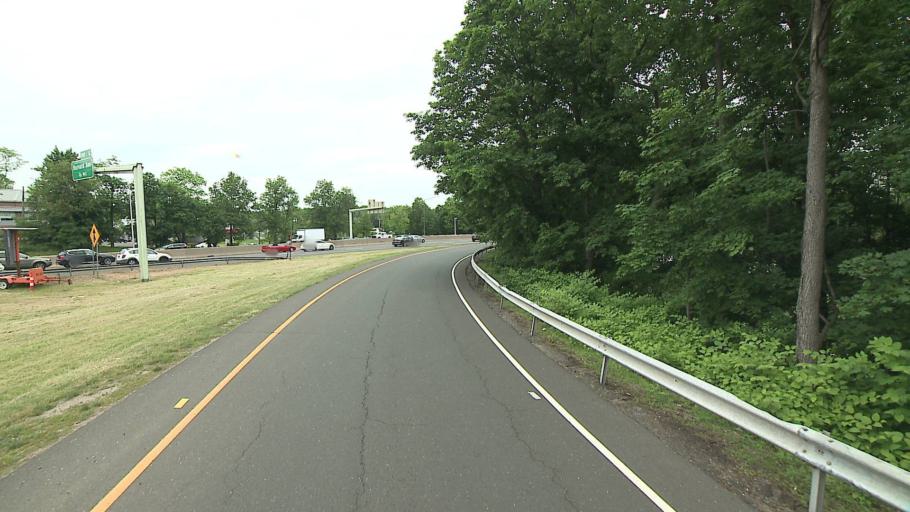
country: US
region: Connecticut
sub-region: Fairfield County
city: Riverside
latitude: 41.0412
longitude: -73.5757
